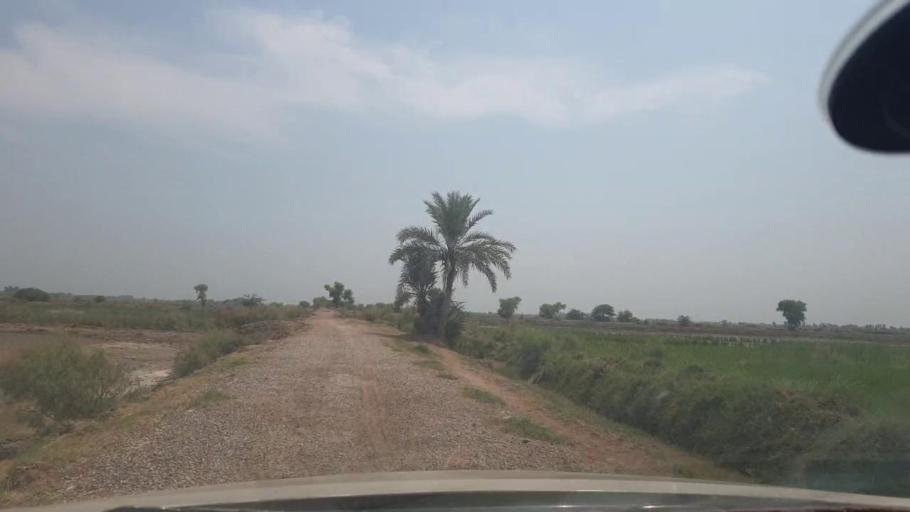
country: PK
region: Sindh
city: Jacobabad
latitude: 28.2279
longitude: 68.3966
